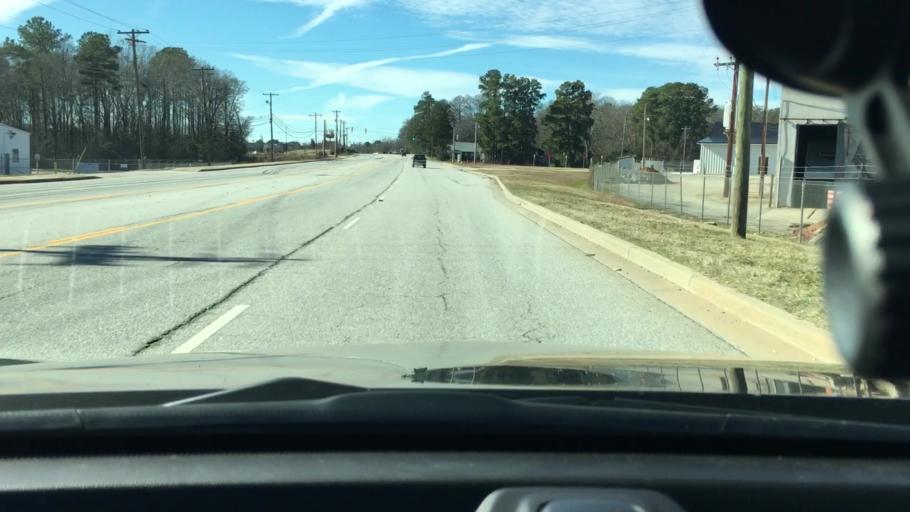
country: US
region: South Carolina
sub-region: Spartanburg County
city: Spartanburg
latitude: 34.9225
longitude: -81.8814
